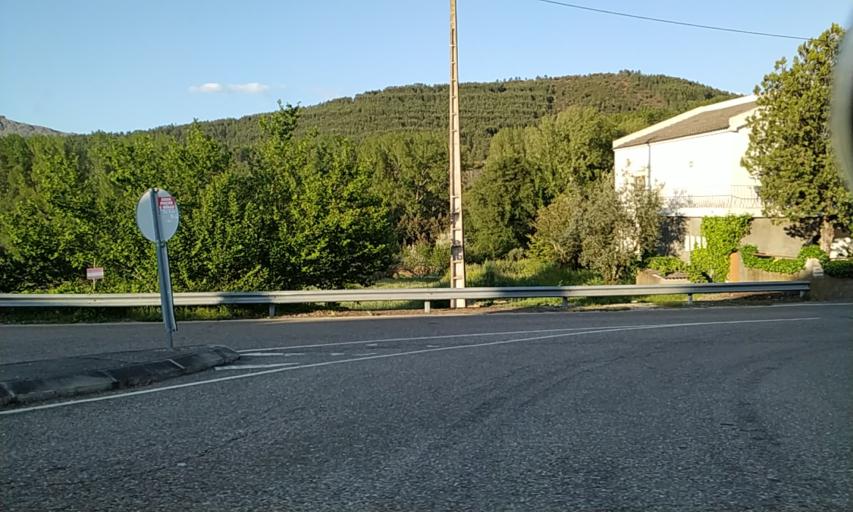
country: PT
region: Portalegre
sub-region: Marvao
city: Marvao
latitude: 39.3724
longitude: -7.3884
